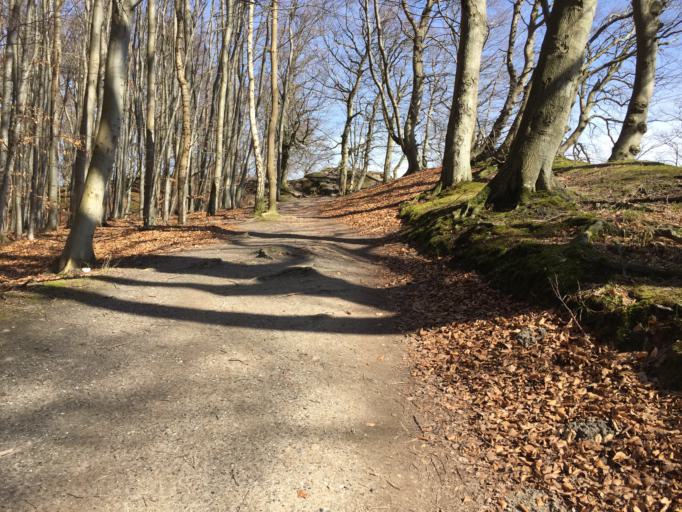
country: DE
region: Mecklenburg-Vorpommern
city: Sassnitz
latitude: 54.5254
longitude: 13.6700
